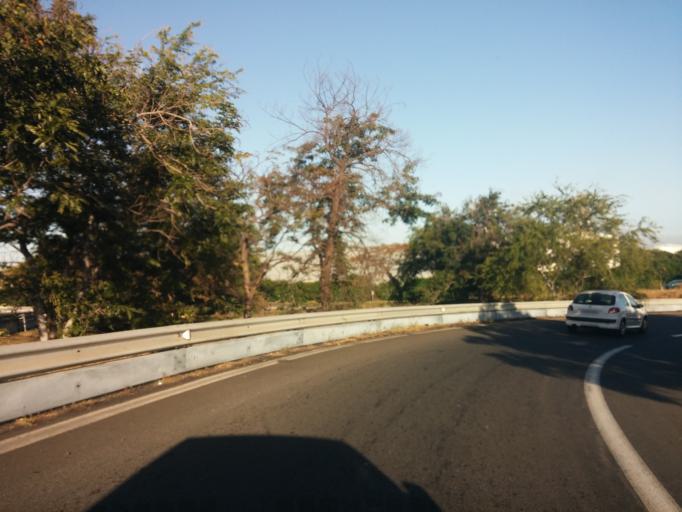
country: RE
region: Reunion
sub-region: Reunion
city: La Possession
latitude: -20.9305
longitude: 55.3320
